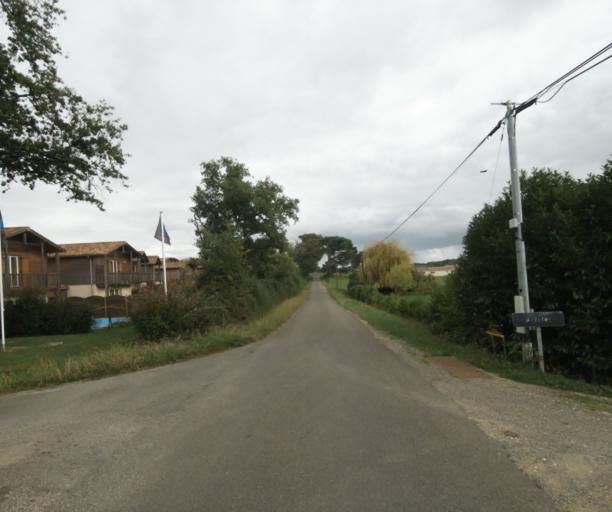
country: FR
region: Midi-Pyrenees
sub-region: Departement du Gers
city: Eauze
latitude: 43.8988
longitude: 0.1134
